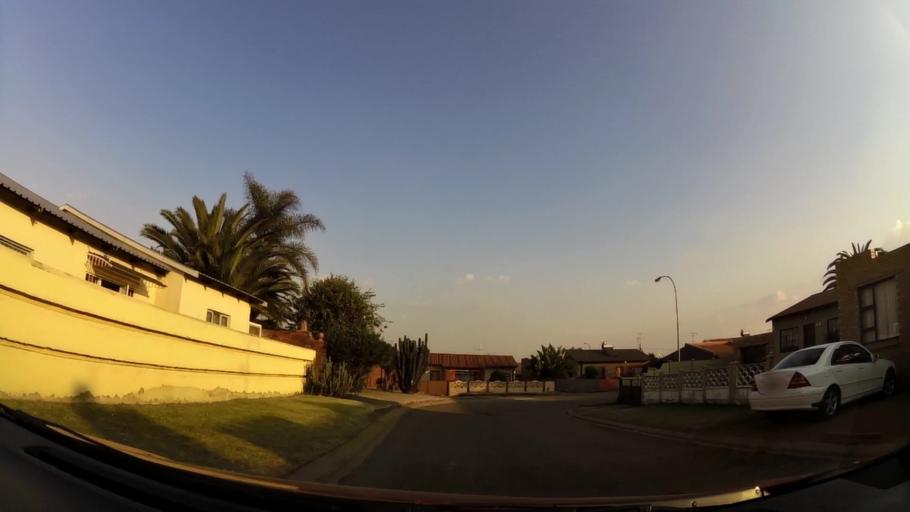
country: ZA
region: Gauteng
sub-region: City of Johannesburg Metropolitan Municipality
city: Soweto
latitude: -26.2852
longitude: 27.9030
